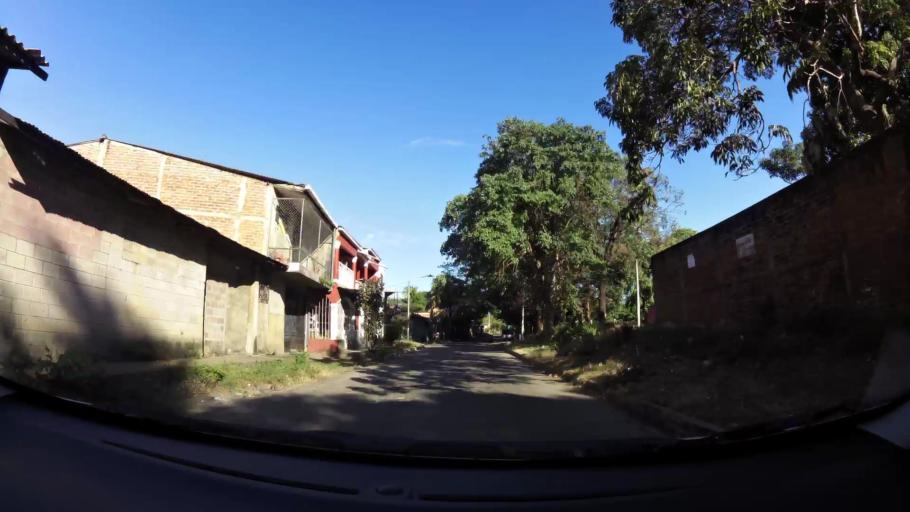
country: SV
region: Sonsonate
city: Sonsonate
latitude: 13.7145
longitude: -89.7182
